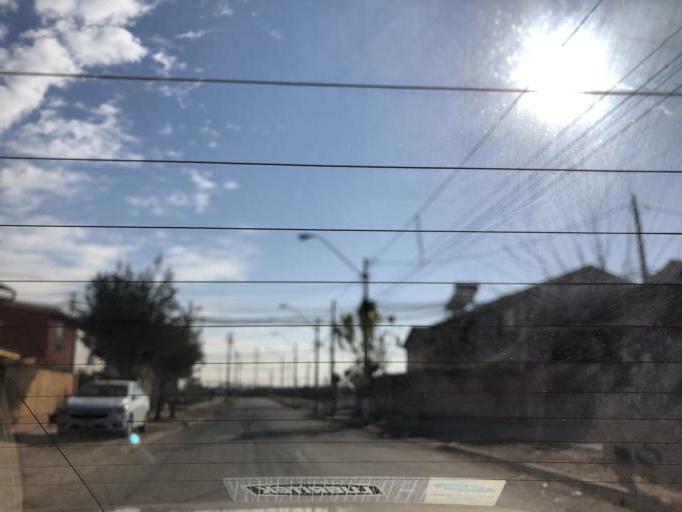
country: CL
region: Santiago Metropolitan
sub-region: Provincia de Cordillera
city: Puente Alto
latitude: -33.6187
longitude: -70.6152
